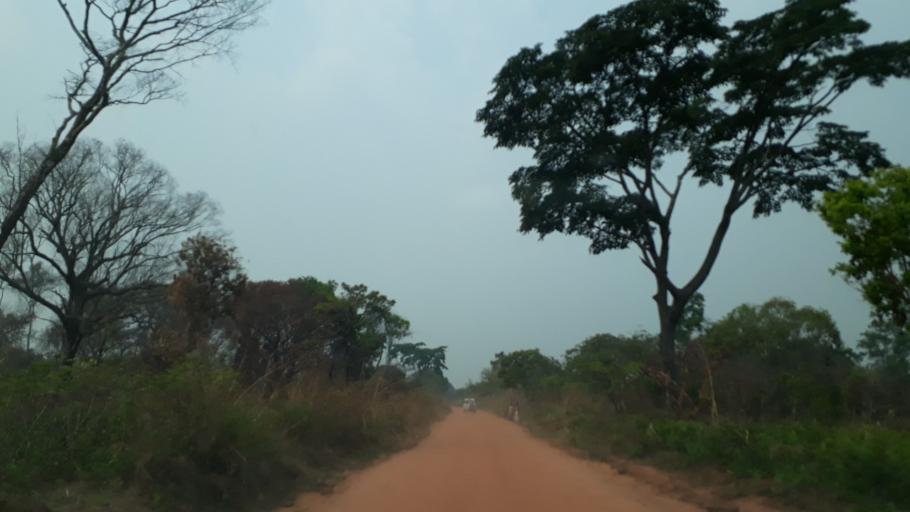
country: CD
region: Kasai-Occidental
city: Tshikapa
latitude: -6.4821
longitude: 20.4325
